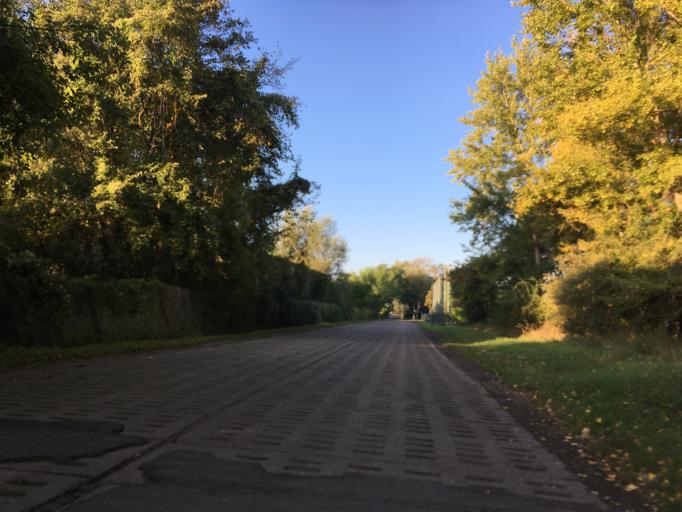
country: DE
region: Brandenburg
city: Frankfurt (Oder)
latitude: 52.3651
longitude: 14.5449
